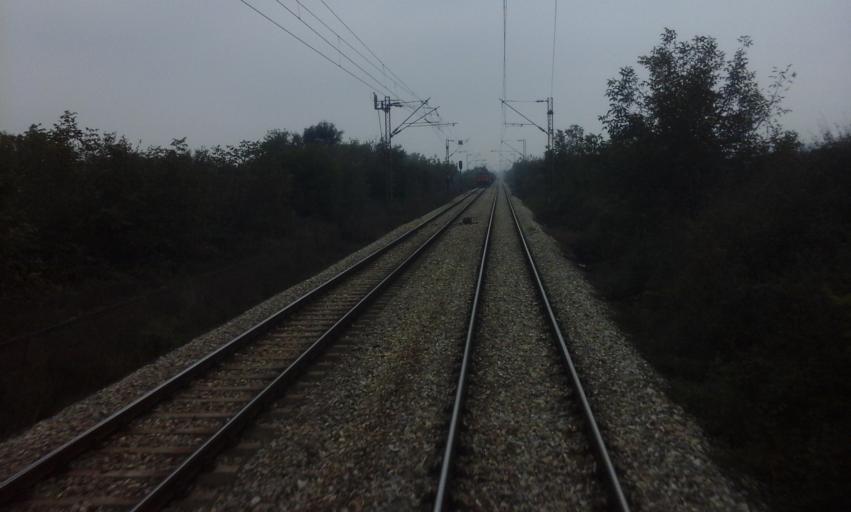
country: RS
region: Central Serbia
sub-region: Sumadijski Okrug
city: Lapovo
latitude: 44.2304
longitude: 21.0958
